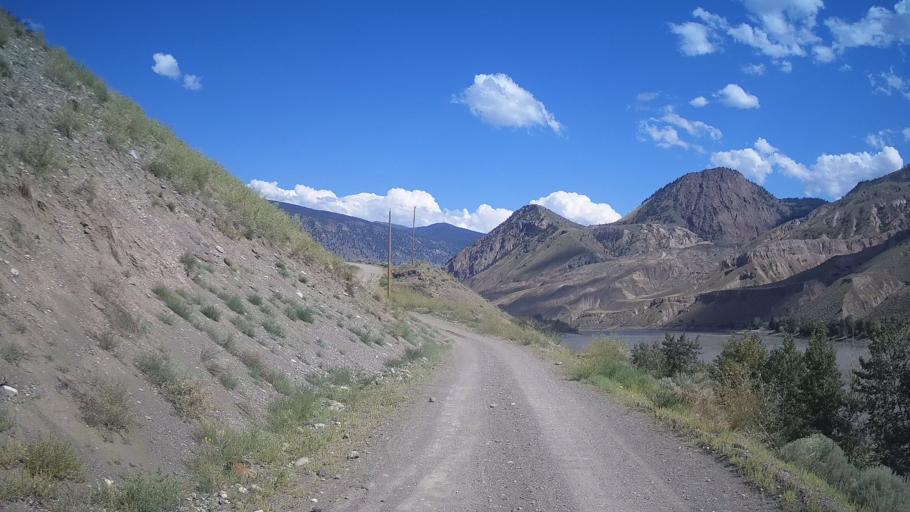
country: CA
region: British Columbia
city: Lillooet
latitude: 51.1819
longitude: -122.1274
